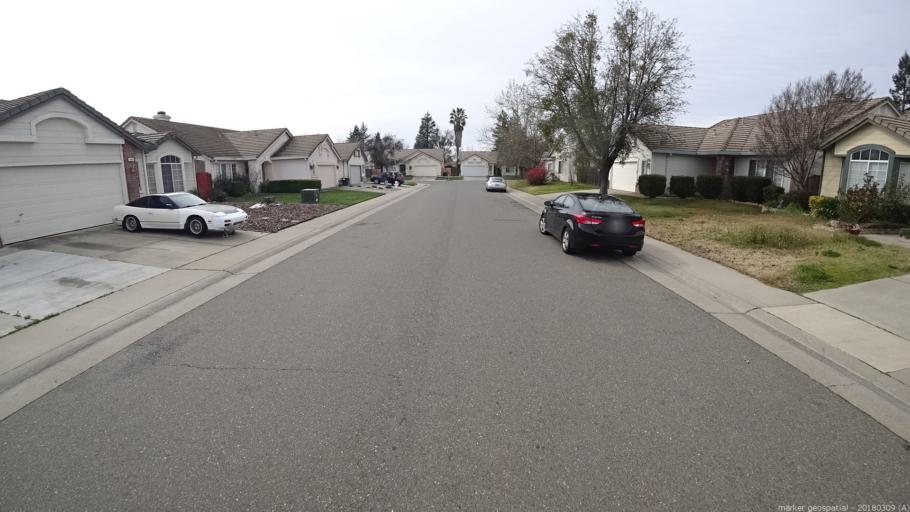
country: US
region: California
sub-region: Sacramento County
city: Vineyard
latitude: 38.4611
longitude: -121.3685
